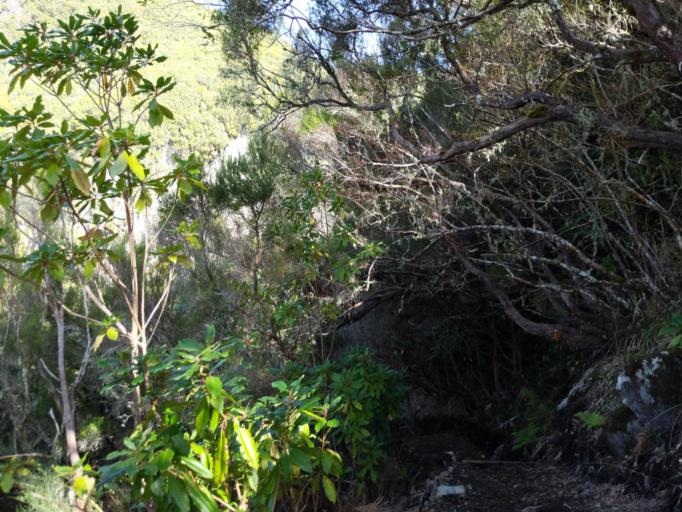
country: PT
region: Madeira
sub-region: Calheta
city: Arco da Calheta
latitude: 32.7647
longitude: -17.1254
